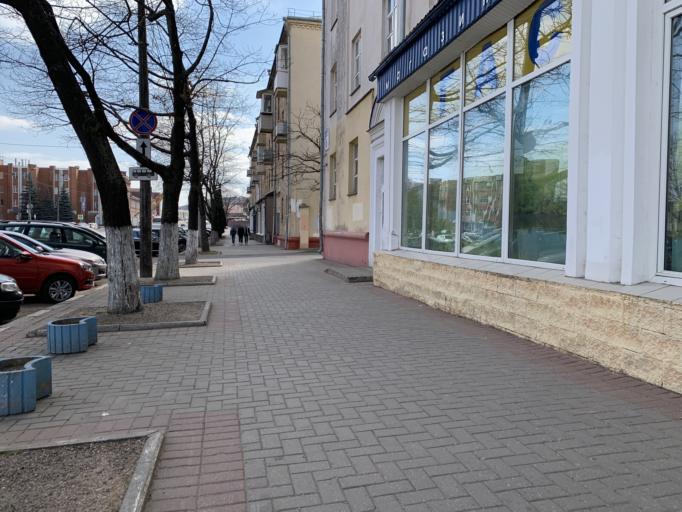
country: BY
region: Minsk
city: Minsk
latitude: 53.8929
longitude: 27.5659
